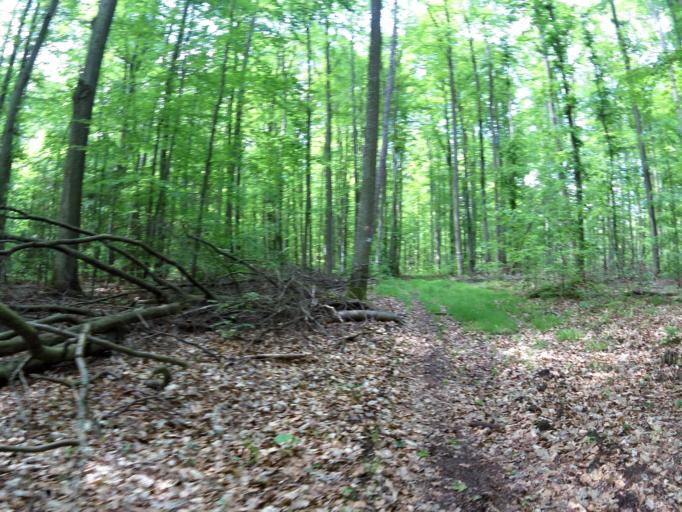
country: DE
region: Bavaria
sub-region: Regierungsbezirk Unterfranken
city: Reichenberg
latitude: 49.7452
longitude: 9.8981
